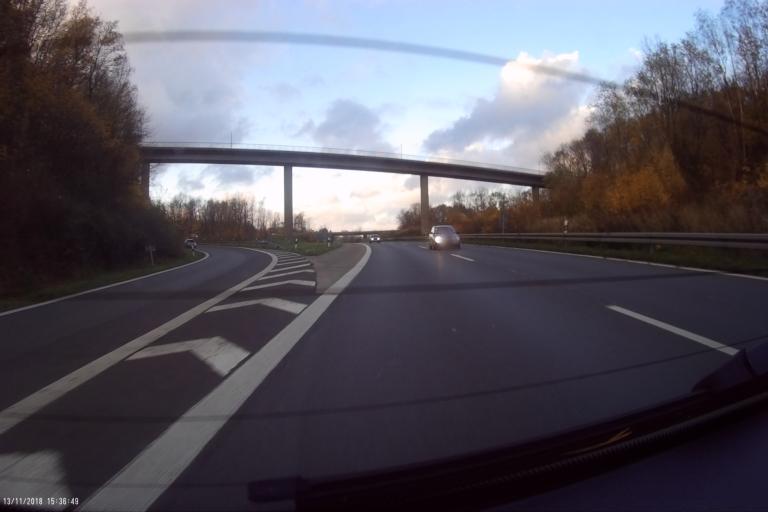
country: DE
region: North Rhine-Westphalia
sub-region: Regierungsbezirk Arnsberg
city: Schwelm
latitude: 51.3112
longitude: 7.2667
